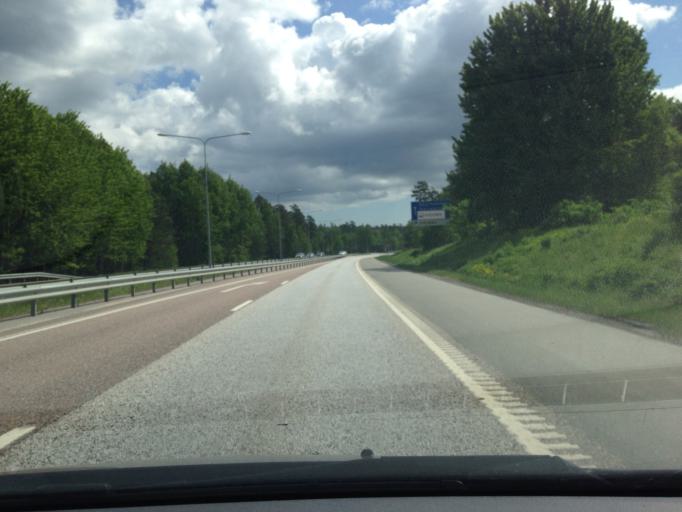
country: SE
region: Stockholm
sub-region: Nacka Kommun
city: Alta
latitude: 59.2438
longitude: 18.1828
